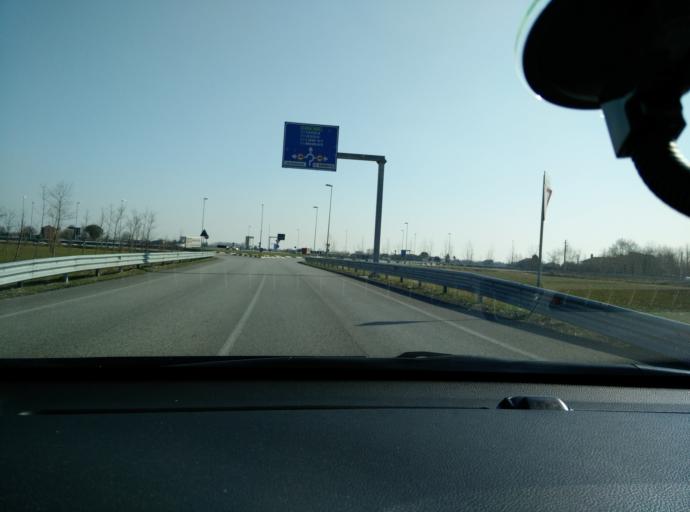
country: IT
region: Veneto
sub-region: Provincia di Treviso
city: Zenson di Piave
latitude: 45.6834
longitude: 12.5103
